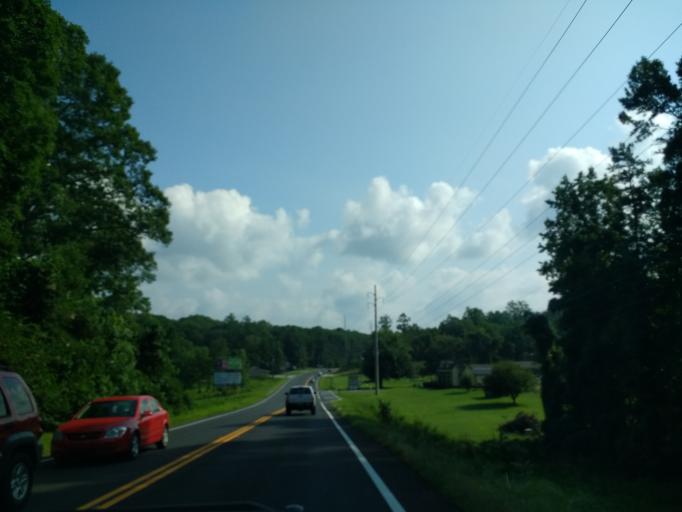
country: US
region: Georgia
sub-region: White County
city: Cleveland
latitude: 34.6464
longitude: -83.7363
